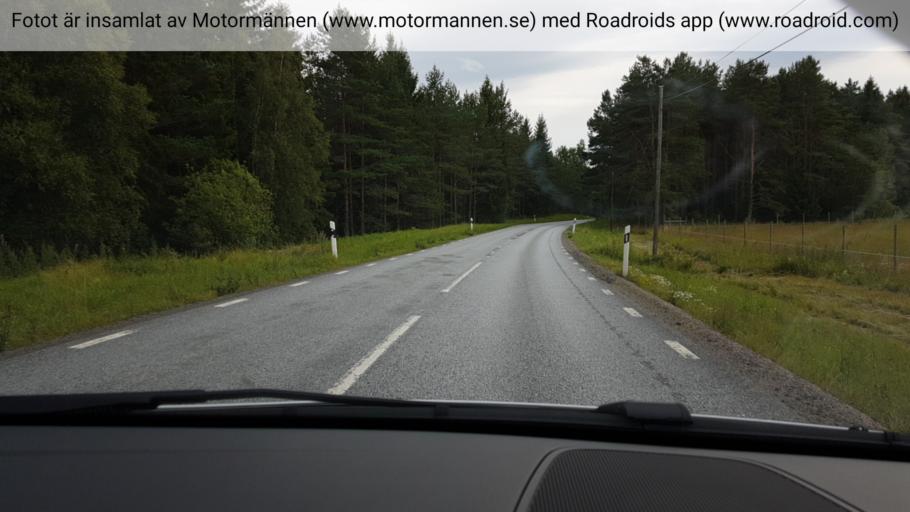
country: SE
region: Uppsala
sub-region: Osthammars Kommun
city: Anneberg
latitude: 60.1633
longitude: 18.4165
